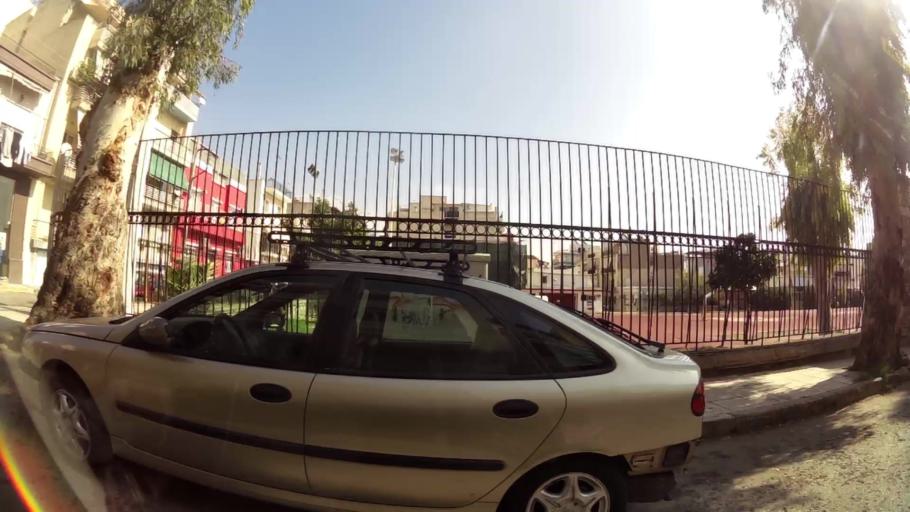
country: GR
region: Attica
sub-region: Nomos Piraios
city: Keratsini
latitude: 37.9597
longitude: 23.6299
